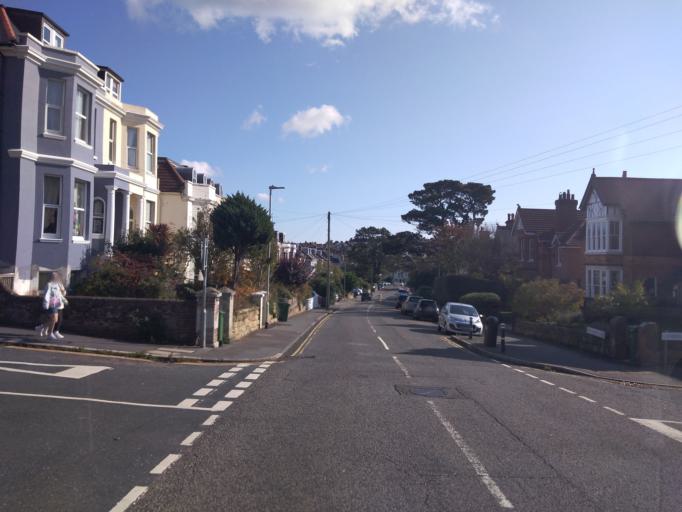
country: GB
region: England
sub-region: East Sussex
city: Saint Leonards-on-Sea
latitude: 50.8633
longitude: 0.5542
